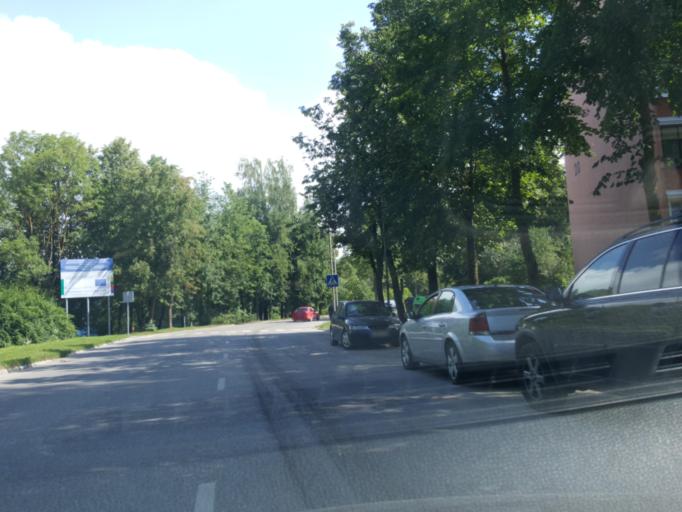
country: LT
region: Alytaus apskritis
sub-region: Alytus
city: Alytus
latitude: 54.4024
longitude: 24.0272
